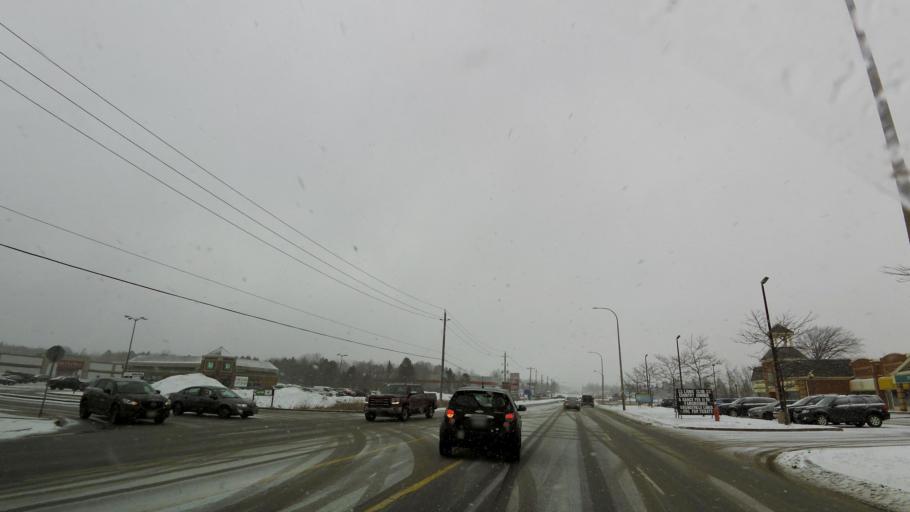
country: CA
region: Ontario
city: Orangeville
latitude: 43.9314
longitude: -80.1005
